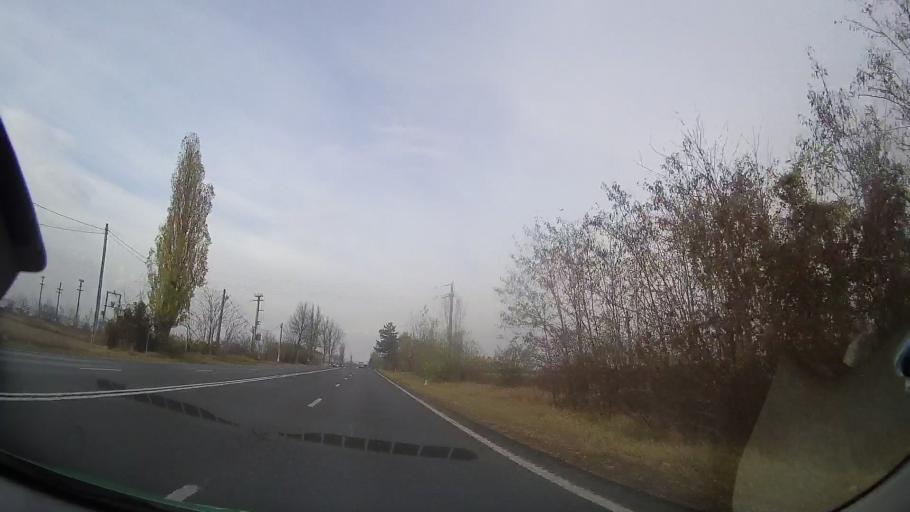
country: RO
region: Prahova
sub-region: Comuna Gorgota
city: Potigrafu
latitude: 44.7684
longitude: 26.1028
